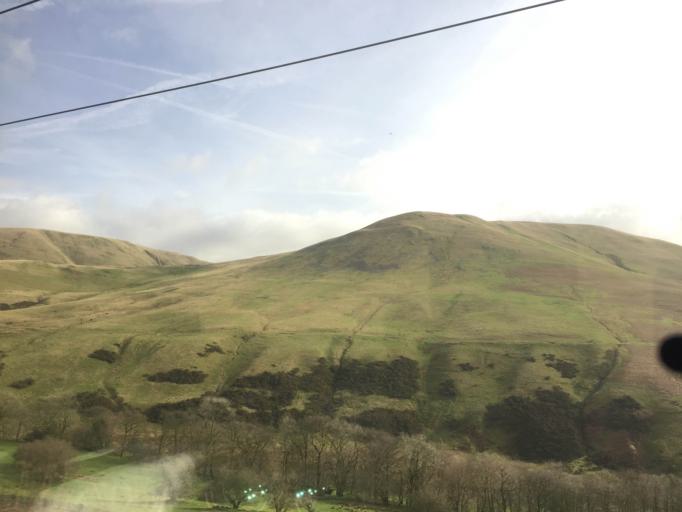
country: GB
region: England
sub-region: Cumbria
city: Sedbergh
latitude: 54.3796
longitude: -2.5807
